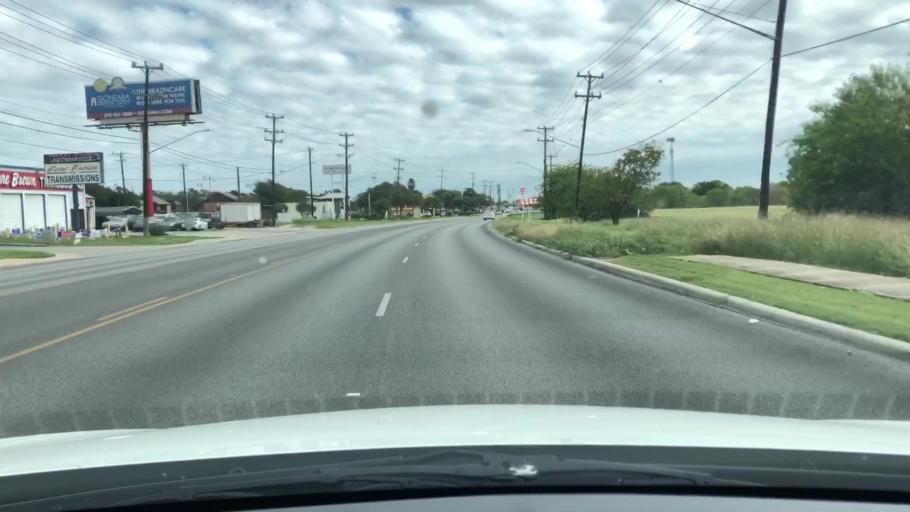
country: US
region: Texas
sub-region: Bexar County
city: Leon Valley
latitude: 29.4830
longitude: -98.6633
